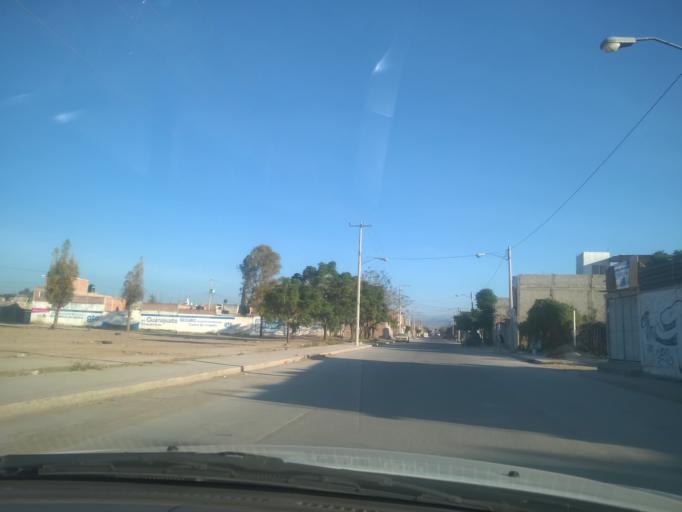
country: MX
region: Guanajuato
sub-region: Leon
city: San Jose de Duran (Los Troncoso)
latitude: 21.0674
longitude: -101.6355
